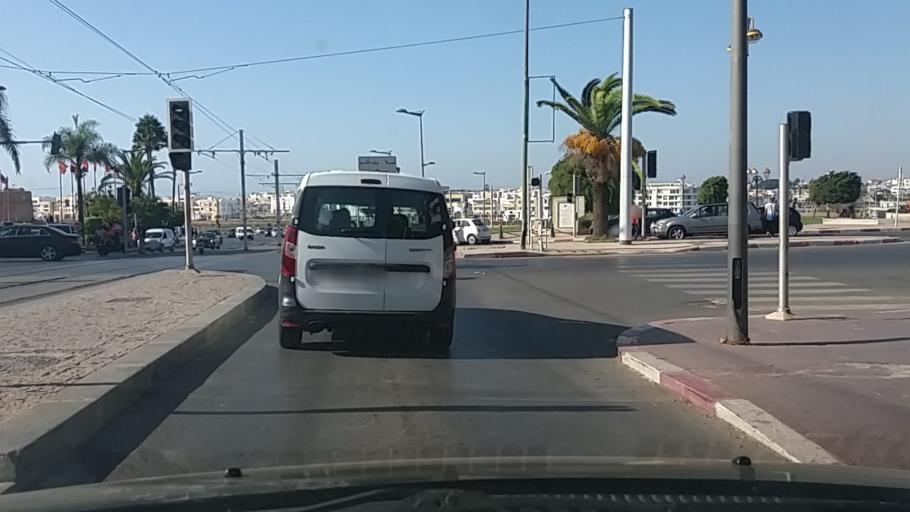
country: MA
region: Rabat-Sale-Zemmour-Zaer
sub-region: Rabat
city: Rabat
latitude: 34.0251
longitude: -6.8252
